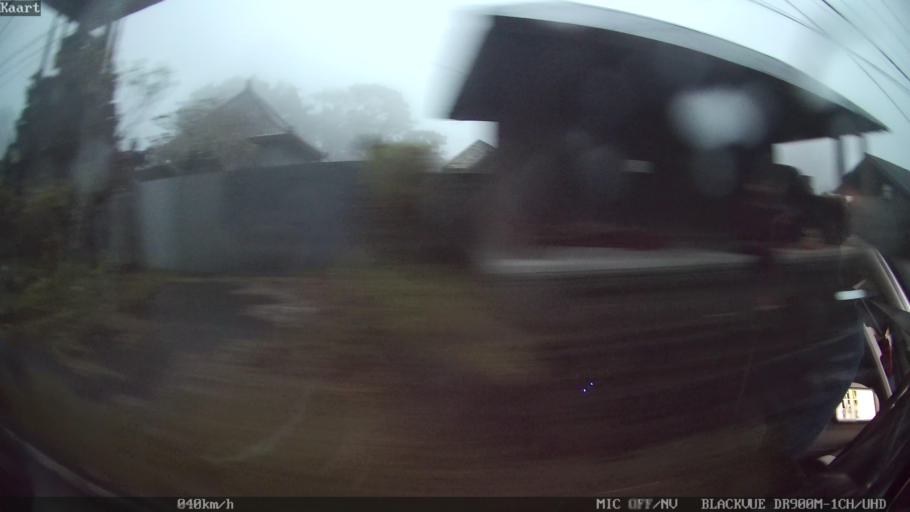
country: ID
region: Bali
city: Banjar Taro Kelod
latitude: -8.3211
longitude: 115.2962
